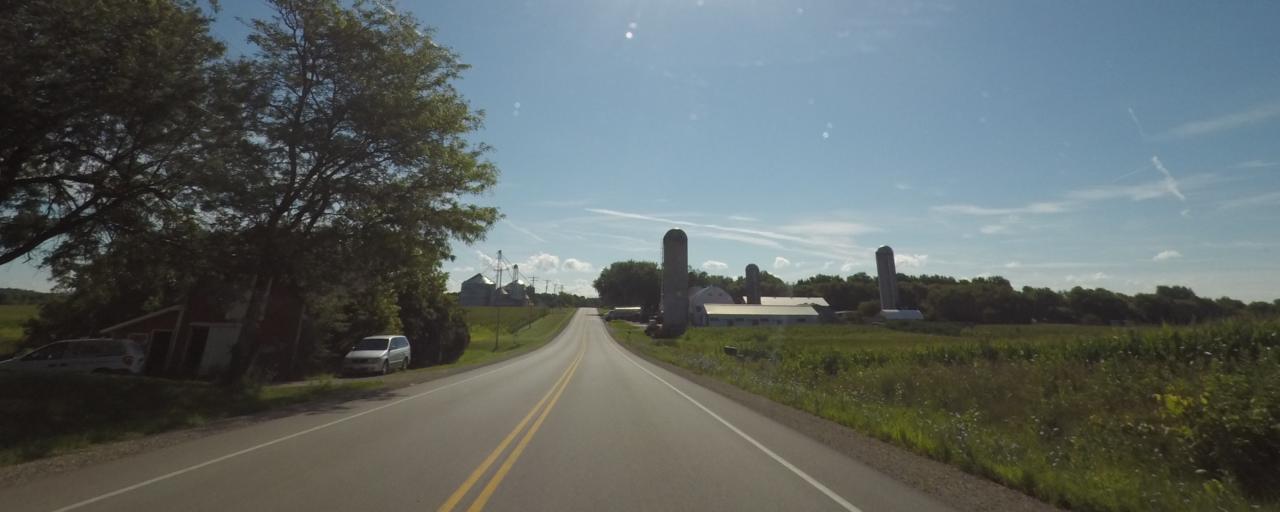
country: US
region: Wisconsin
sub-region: Jefferson County
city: Johnson Creek
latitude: 43.0756
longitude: -88.7261
